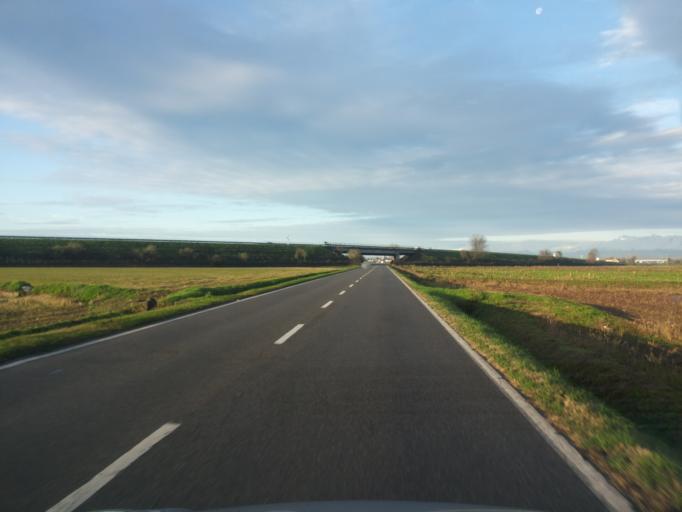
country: IT
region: Piedmont
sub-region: Provincia di Vercelli
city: Crova
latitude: 45.3450
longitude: 8.2078
